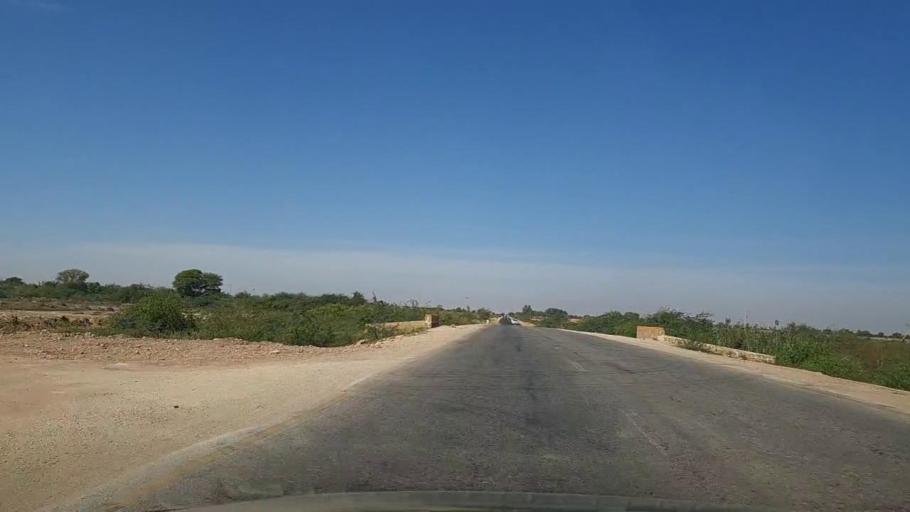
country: PK
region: Sindh
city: Kotri
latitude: 25.2226
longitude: 68.2376
